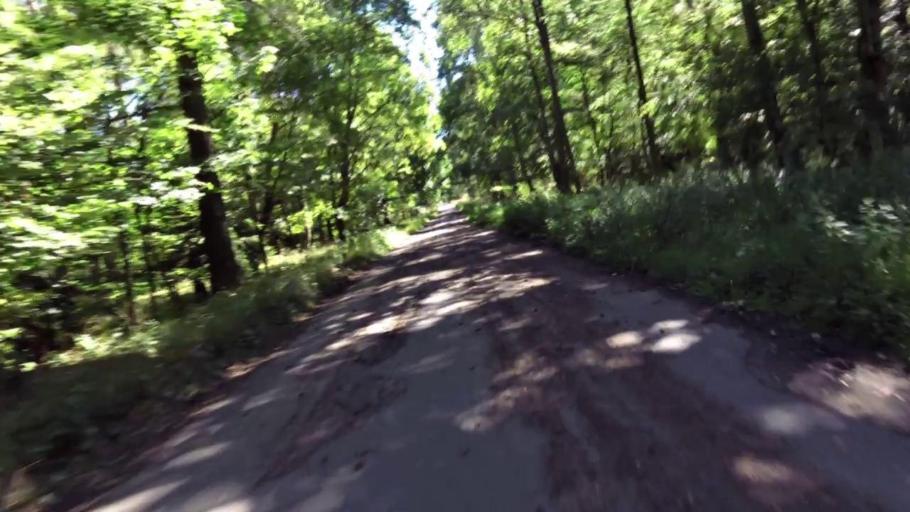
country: PL
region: West Pomeranian Voivodeship
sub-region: Powiat szczecinecki
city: Borne Sulinowo
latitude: 53.6007
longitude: 16.6104
